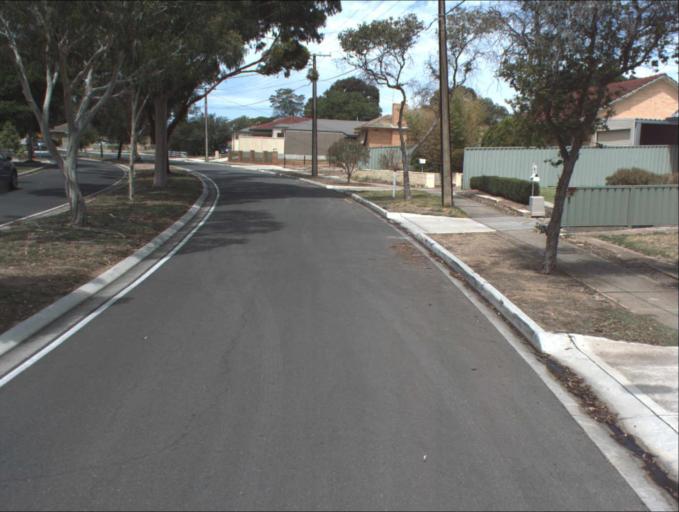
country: AU
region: South Australia
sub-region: Port Adelaide Enfield
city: Enfield
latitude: -34.8534
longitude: 138.6118
